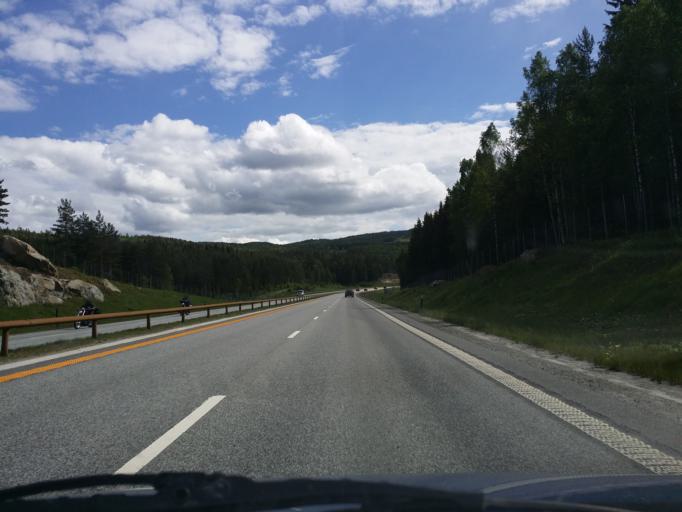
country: NO
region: Hedmark
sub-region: Stange
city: Stange
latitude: 60.6122
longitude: 11.3058
